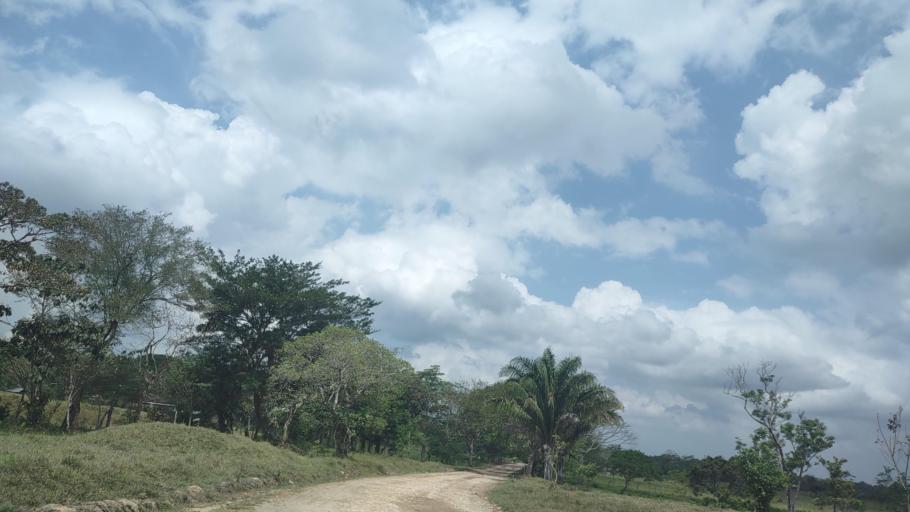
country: MX
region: Veracruz
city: Las Choapas
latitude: 17.9601
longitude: -94.1191
